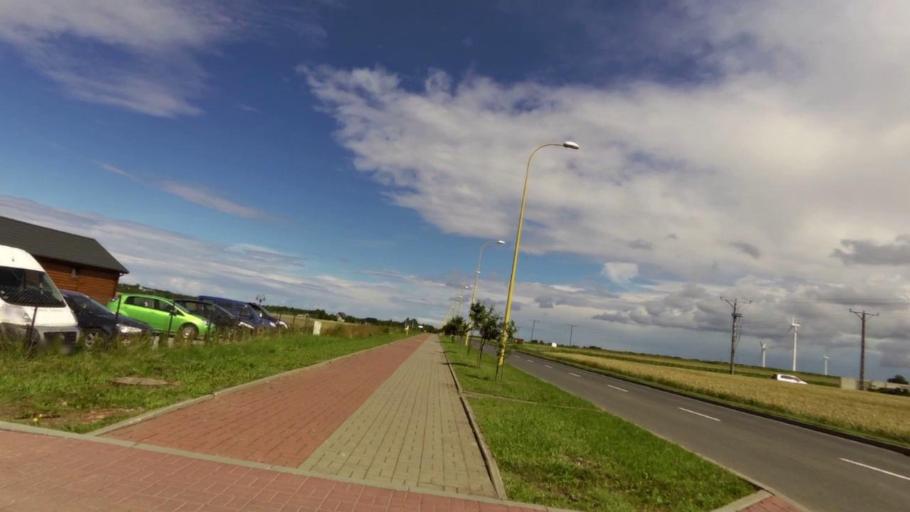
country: PL
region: West Pomeranian Voivodeship
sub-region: Powiat slawienski
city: Darlowo
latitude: 54.4372
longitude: 16.4092
